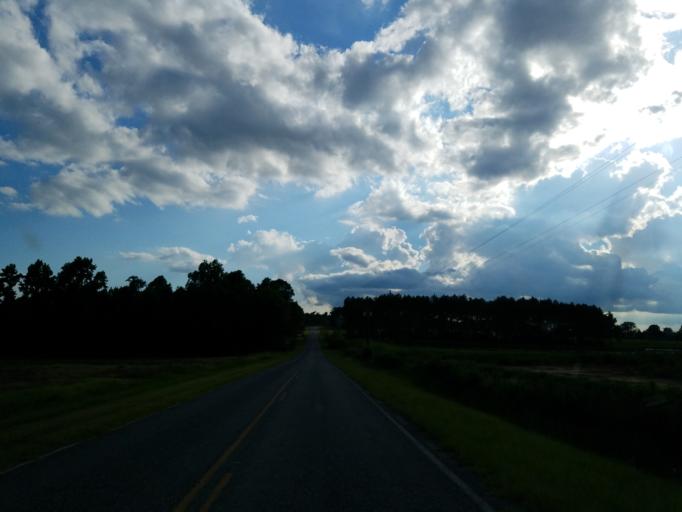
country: US
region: Georgia
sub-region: Turner County
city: Ashburn
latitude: 31.6208
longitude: -83.6001
